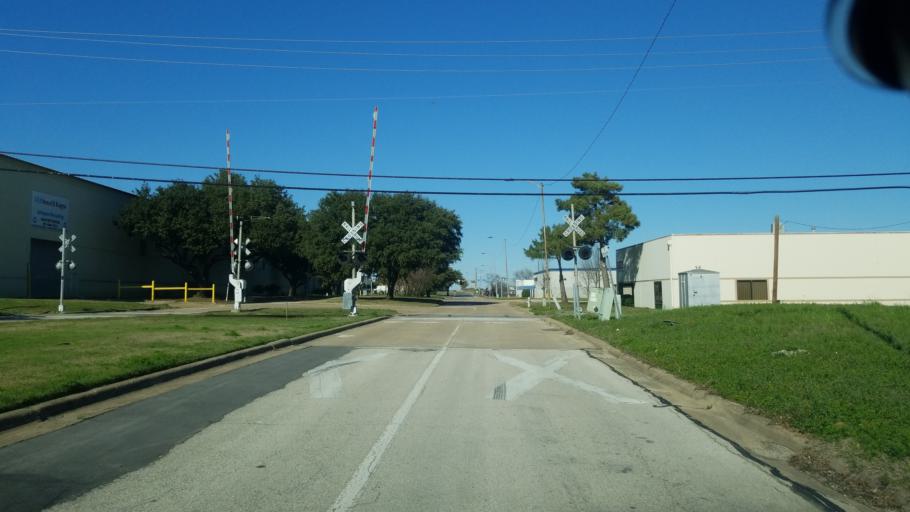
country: US
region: Texas
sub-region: Tarrant County
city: Arlington
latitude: 32.7468
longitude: -97.0542
